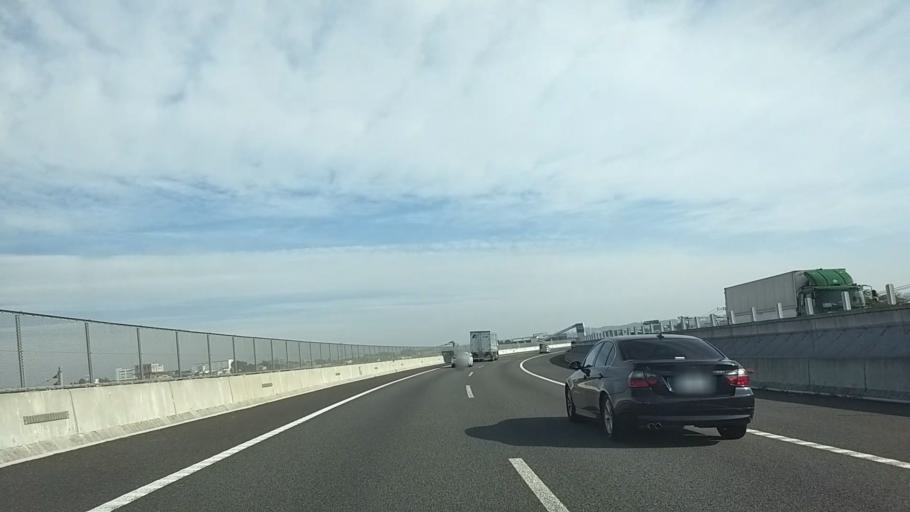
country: JP
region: Kanagawa
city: Atsugi
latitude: 35.4579
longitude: 139.3721
